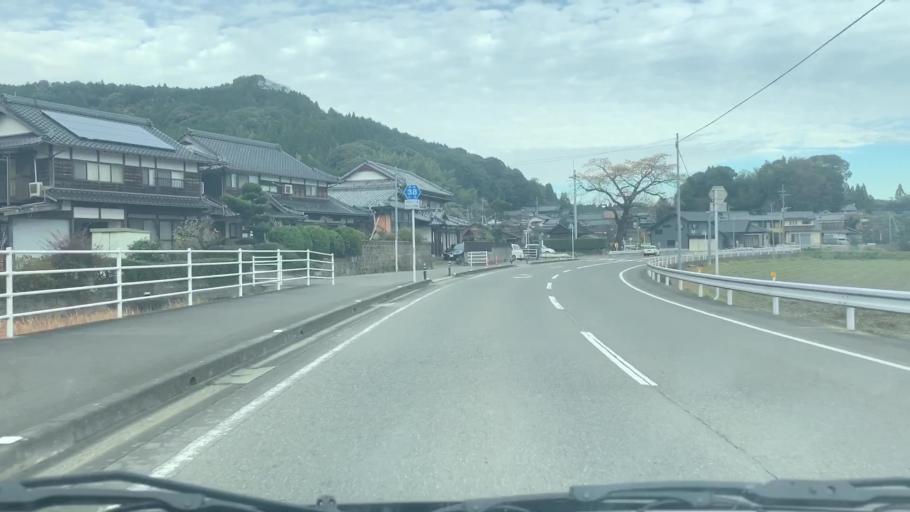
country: JP
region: Saga Prefecture
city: Takeocho-takeo
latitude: 33.1997
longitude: 129.9608
